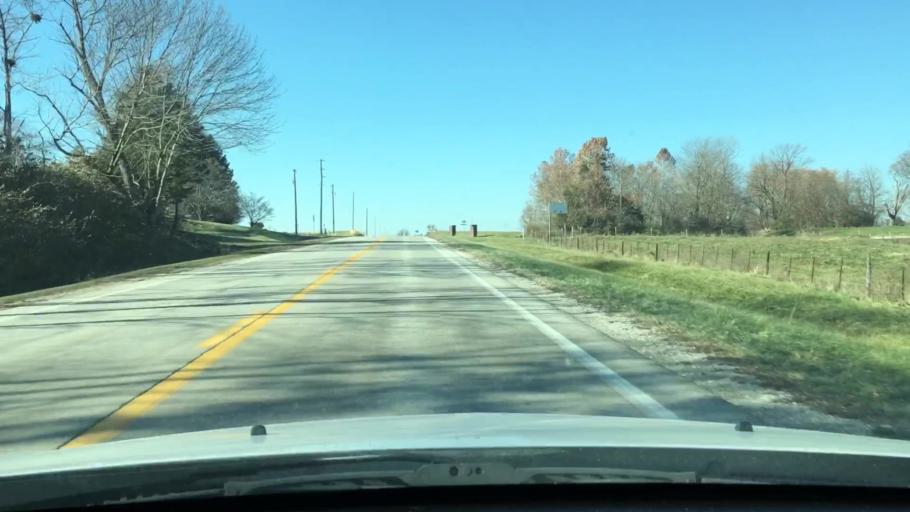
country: US
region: Illinois
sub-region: Pike County
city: Griggsville
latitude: 39.6194
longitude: -90.7118
